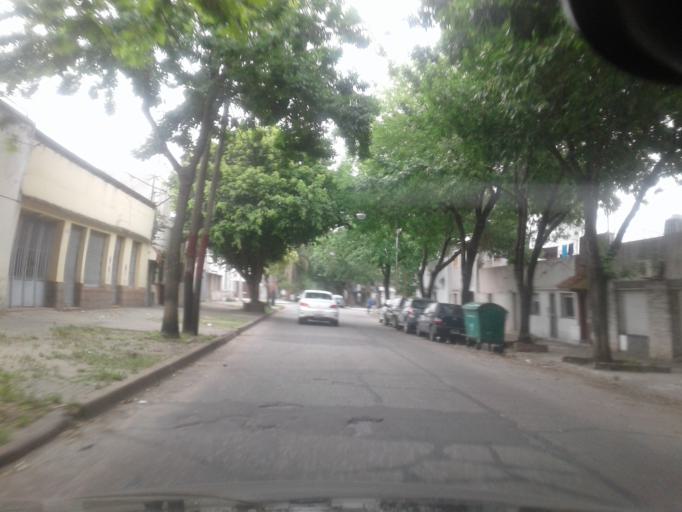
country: AR
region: Santa Fe
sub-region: Departamento de Rosario
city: Rosario
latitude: -32.9655
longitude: -60.6622
